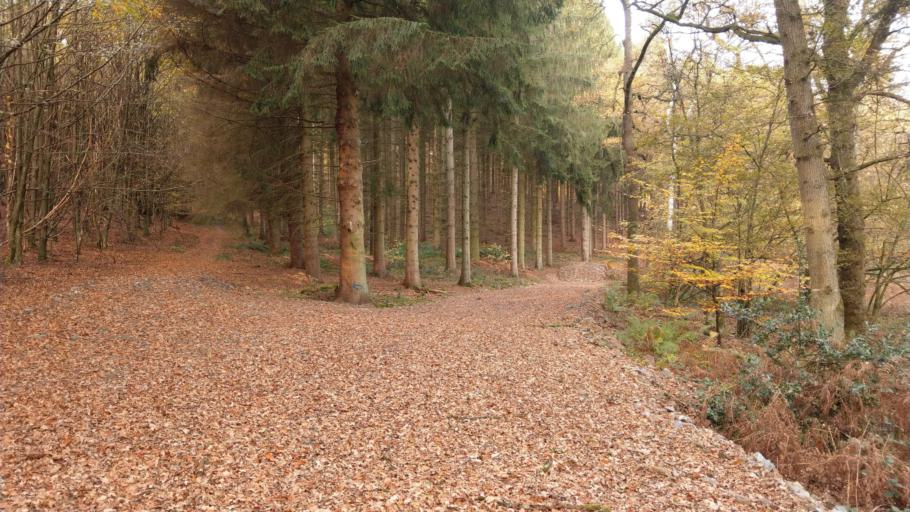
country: BE
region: Wallonia
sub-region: Province de Liege
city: La Calamine
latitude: 50.7360
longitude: 6.0206
